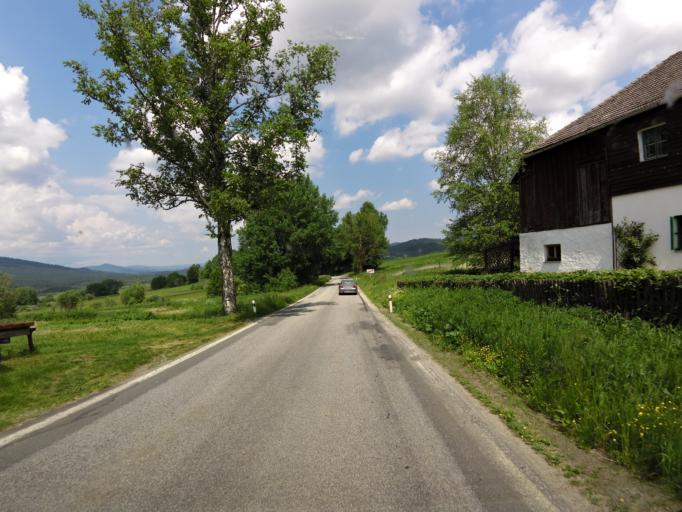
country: CZ
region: Jihocesky
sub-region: Okres Cesky Krumlov
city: Horni Plana
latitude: 48.8212
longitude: 13.9663
